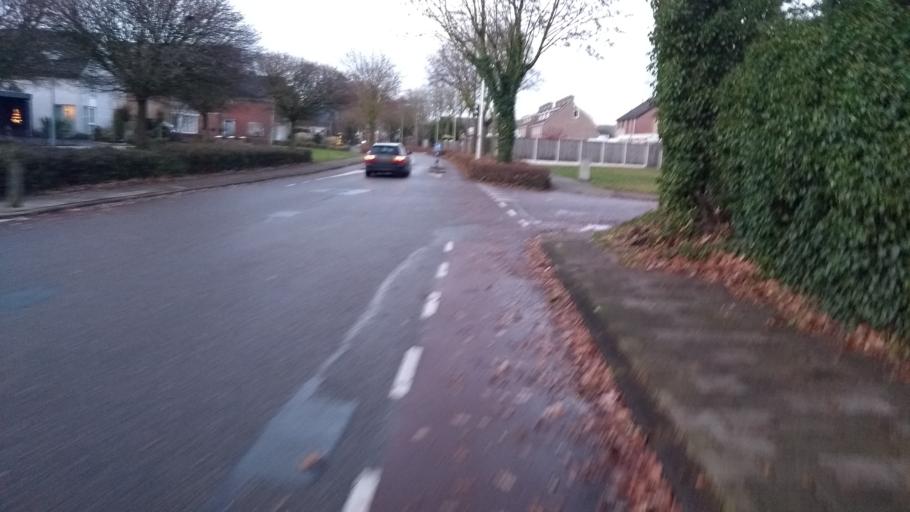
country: NL
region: Overijssel
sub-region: Gemeente Almelo
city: Almelo
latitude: 52.3755
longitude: 6.6890
